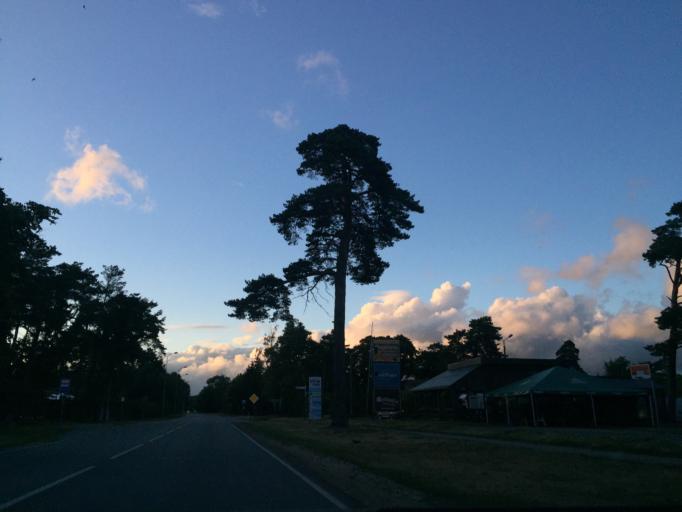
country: LV
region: Saulkrastu
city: Saulkrasti
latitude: 57.2979
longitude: 24.4099
